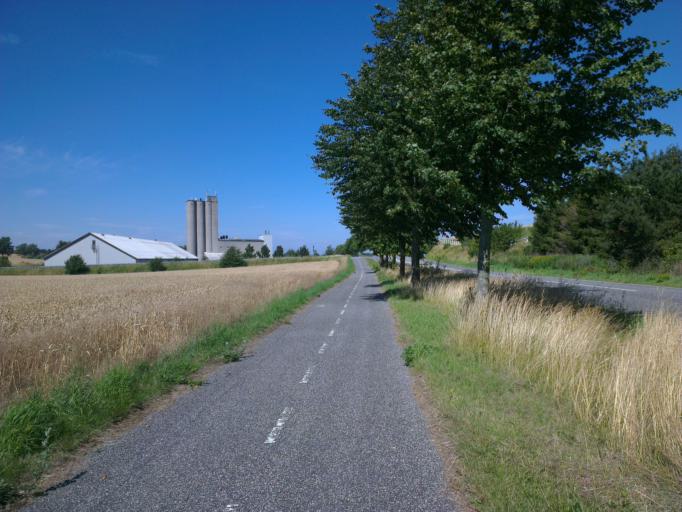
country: DK
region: Capital Region
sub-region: Frederikssund Kommune
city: Slangerup
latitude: 55.8314
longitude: 12.1860
